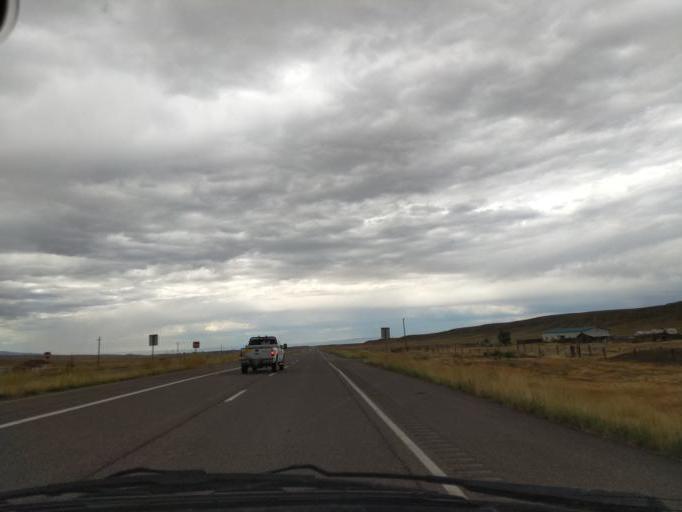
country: US
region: Colorado
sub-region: Mesa County
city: Palisade
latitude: 38.8864
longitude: -108.3575
